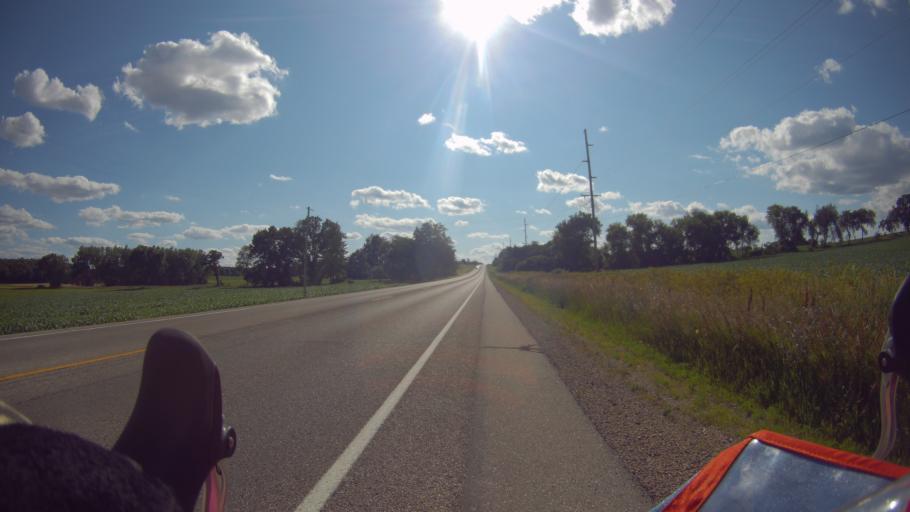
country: US
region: Wisconsin
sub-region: Dane County
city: Oregon
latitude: 42.9186
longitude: -89.3236
